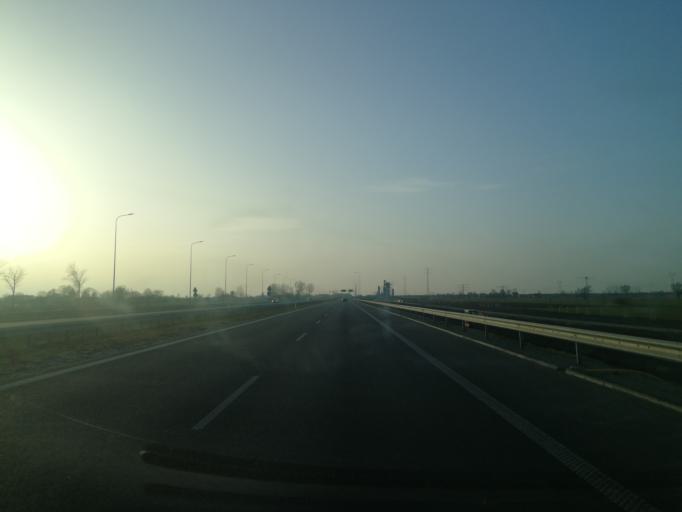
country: PL
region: Pomeranian Voivodeship
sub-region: Powiat nowodworski
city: Ostaszewo
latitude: 54.2540
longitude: 18.9699
